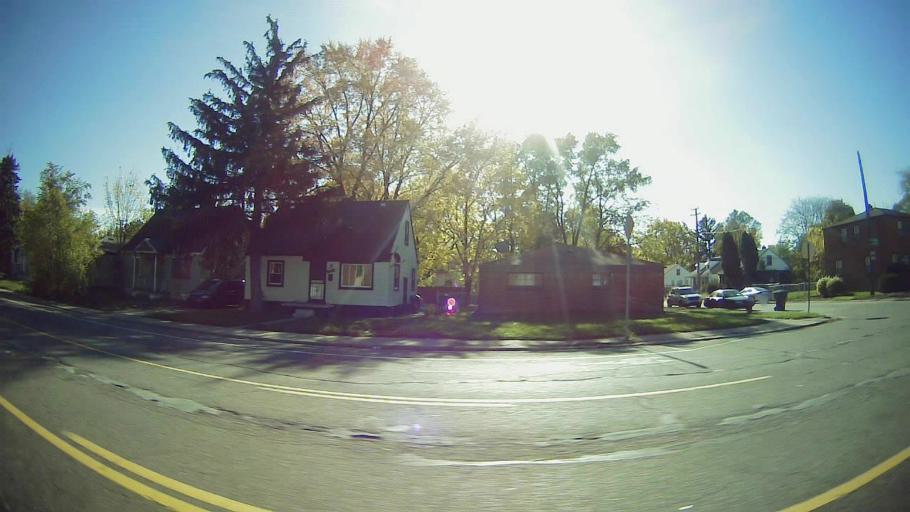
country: US
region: Michigan
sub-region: Wayne County
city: Dearborn
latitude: 42.3655
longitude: -83.1941
